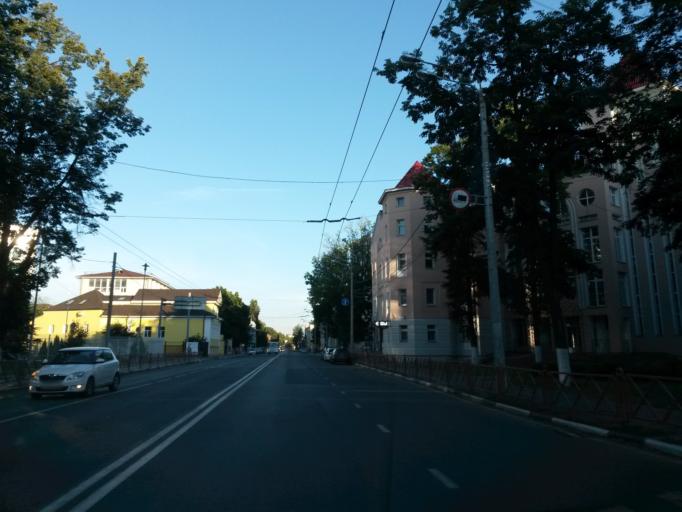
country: RU
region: Jaroslavl
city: Yaroslavl
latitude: 57.6356
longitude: 39.8815
